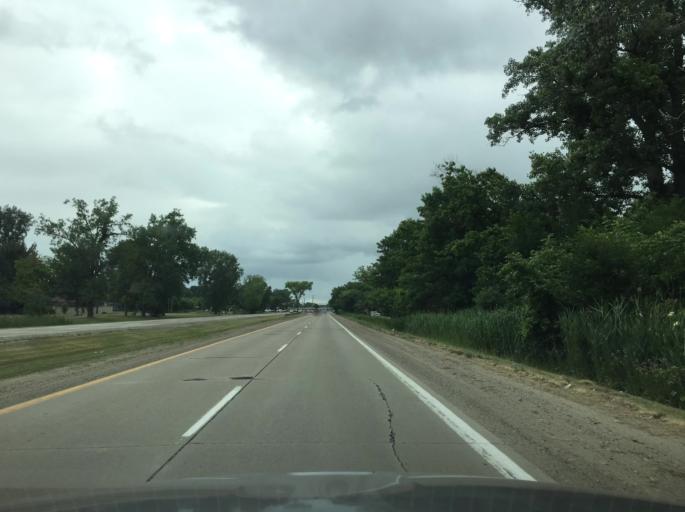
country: US
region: Michigan
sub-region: Macomb County
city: Mount Clemens
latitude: 42.5736
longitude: -82.8476
